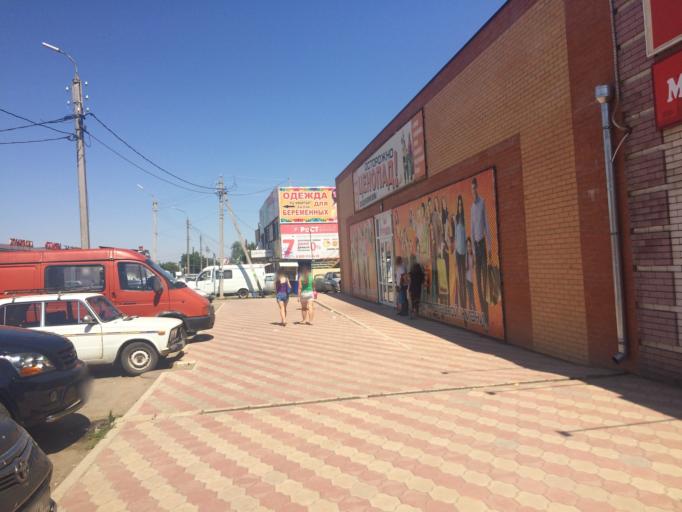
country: RU
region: Rostov
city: Sal'sk
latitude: 46.4706
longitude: 41.5347
